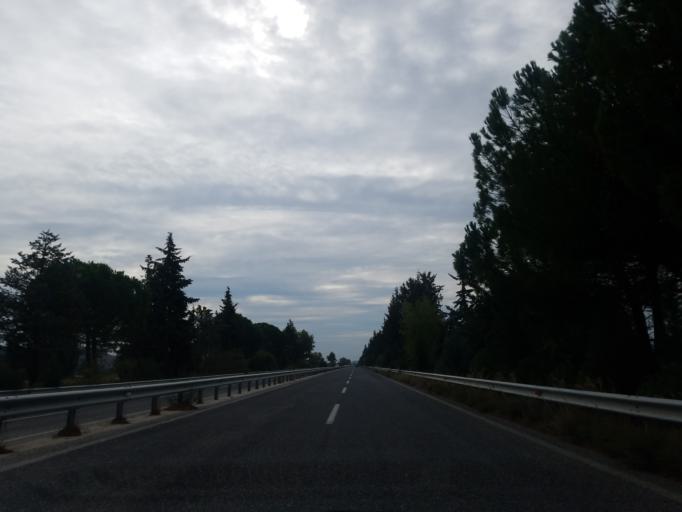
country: GR
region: Thessaly
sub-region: Trikala
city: Vasiliki
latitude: 39.6457
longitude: 21.6889
